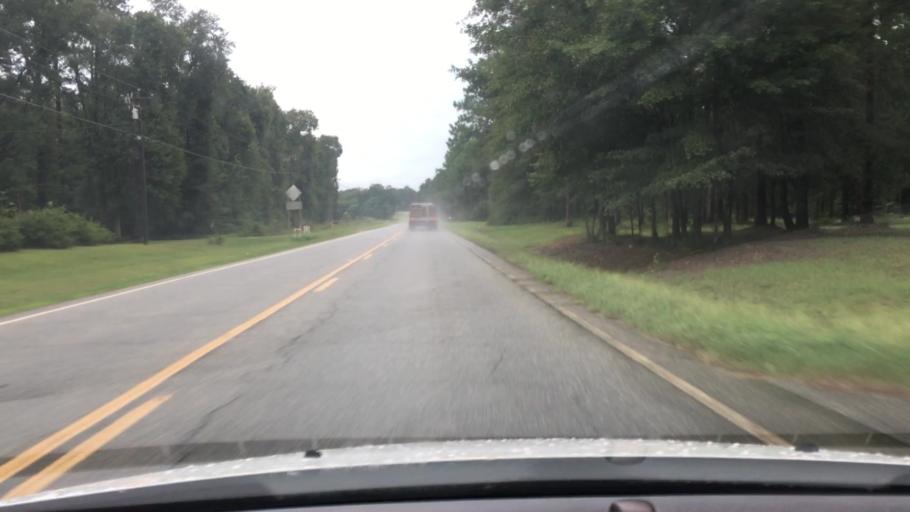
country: US
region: Georgia
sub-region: Grady County
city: Cairo
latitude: 30.7873
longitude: -84.2714
